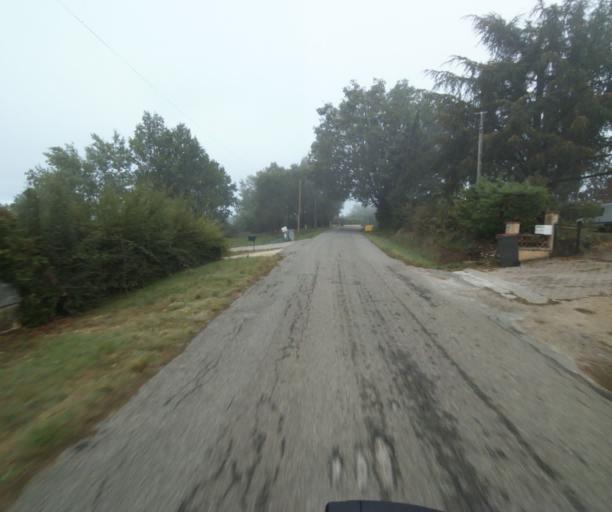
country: FR
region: Midi-Pyrenees
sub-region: Departement du Tarn-et-Garonne
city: Corbarieu
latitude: 43.9474
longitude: 1.3983
